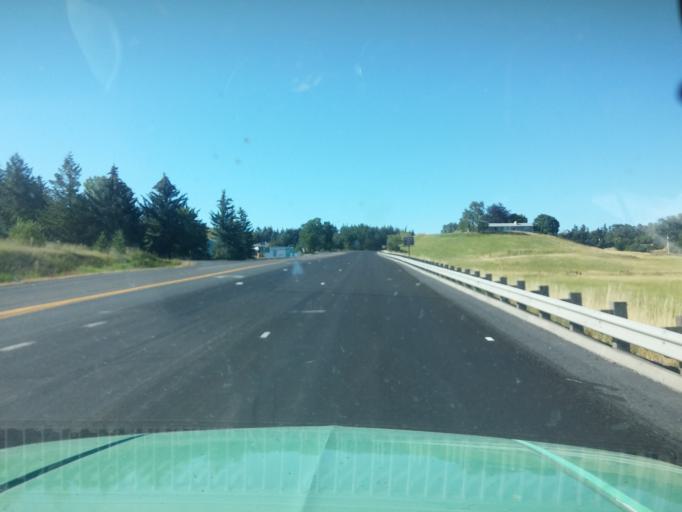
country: US
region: Idaho
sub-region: Latah County
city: Moscow
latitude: 46.6977
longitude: -117.0079
